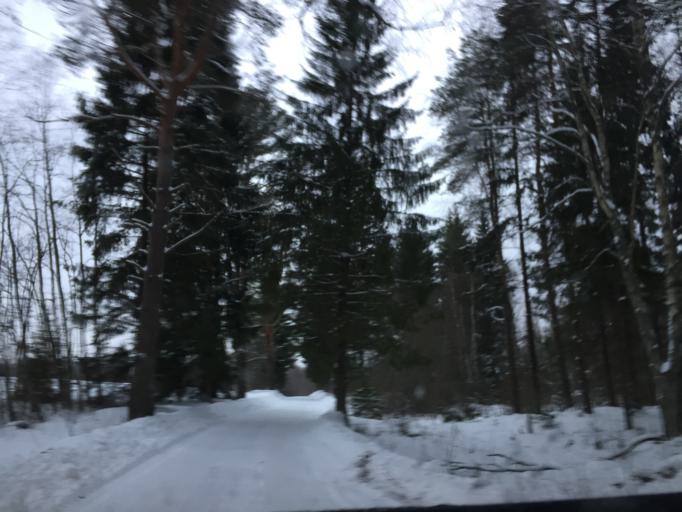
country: LV
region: Amatas Novads
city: Drabesi
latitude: 57.2045
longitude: 25.2980
